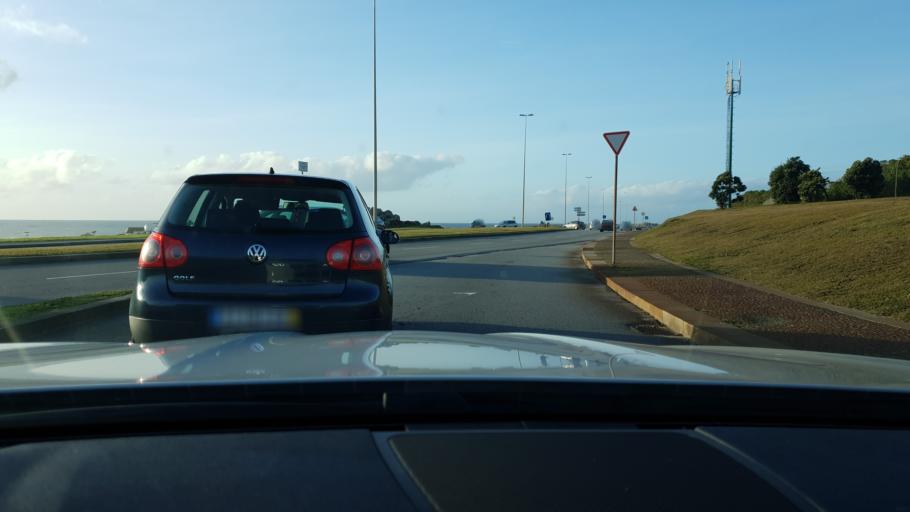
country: PT
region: Porto
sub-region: Matosinhos
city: Leca da Palmeira
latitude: 41.2018
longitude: -8.7112
